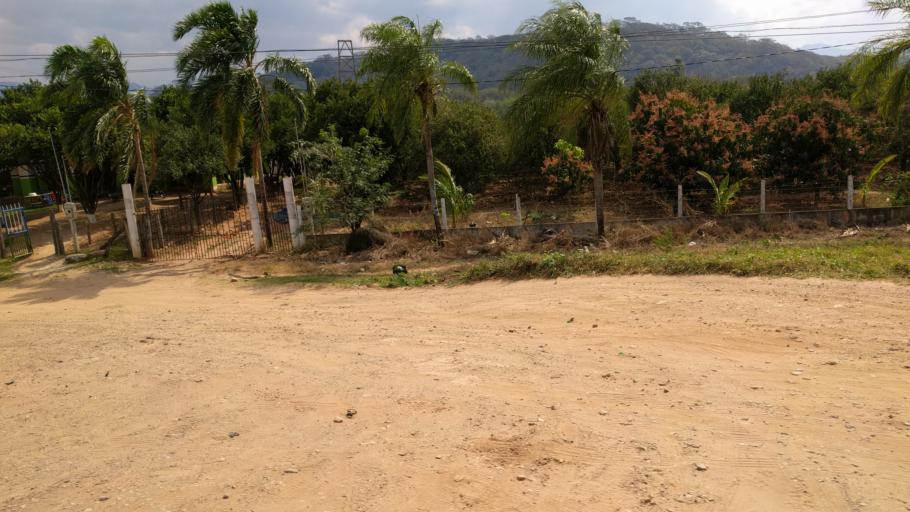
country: BO
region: Santa Cruz
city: Jorochito
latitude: -18.1057
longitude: -63.4564
